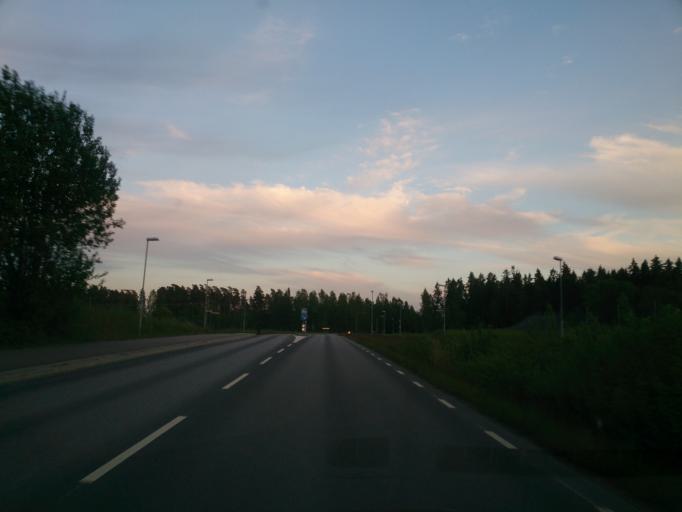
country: SE
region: OEstergoetland
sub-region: Linkopings Kommun
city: Malmslatt
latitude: 58.4049
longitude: 15.5529
